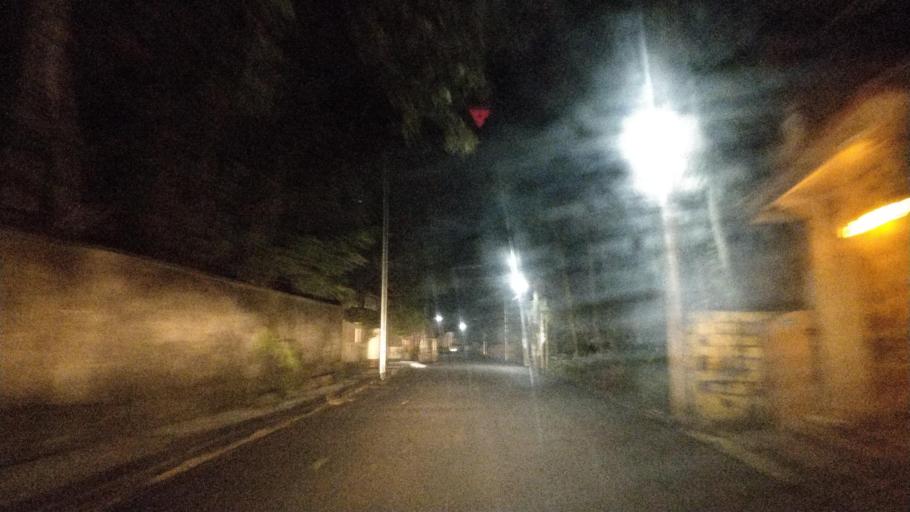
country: IN
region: Kerala
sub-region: Kottayam
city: Kottayam
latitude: 9.6425
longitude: 76.5126
